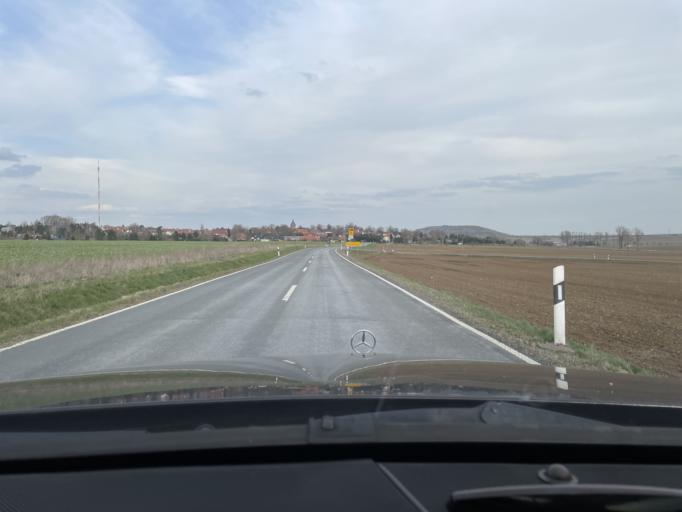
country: DE
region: Thuringia
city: Vollenborn
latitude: 51.3310
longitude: 10.5154
